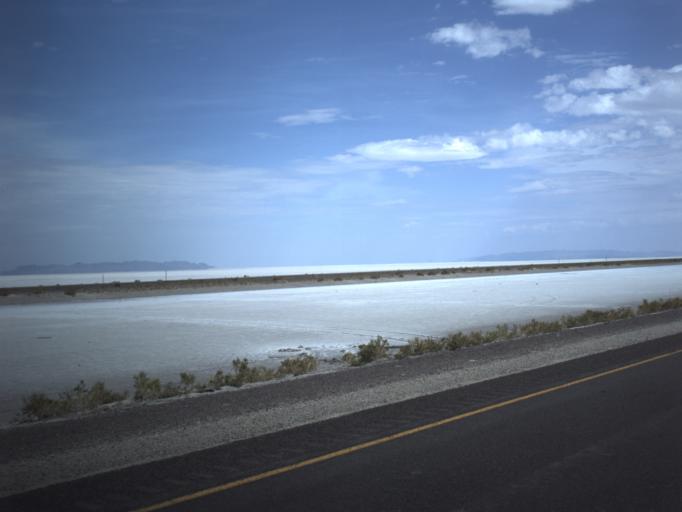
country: US
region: Utah
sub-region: Tooele County
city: Wendover
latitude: 40.7358
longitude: -113.7194
